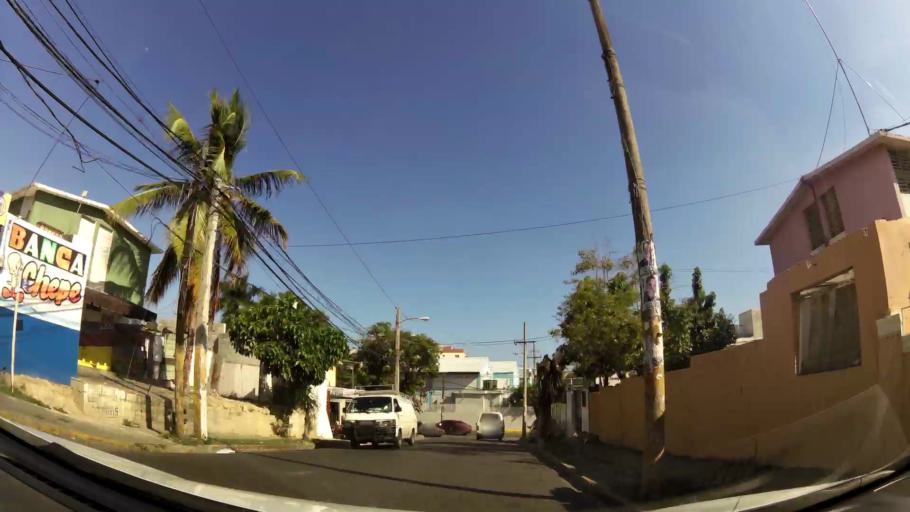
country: DO
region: Nacional
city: Santo Domingo
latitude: 18.4732
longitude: -69.9920
